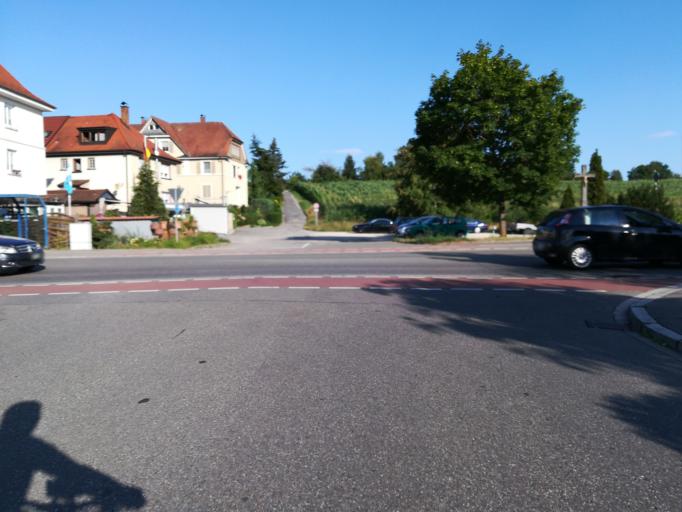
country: DE
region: Baden-Wuerttemberg
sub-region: Freiburg Region
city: Singen
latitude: 47.7563
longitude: 8.8212
